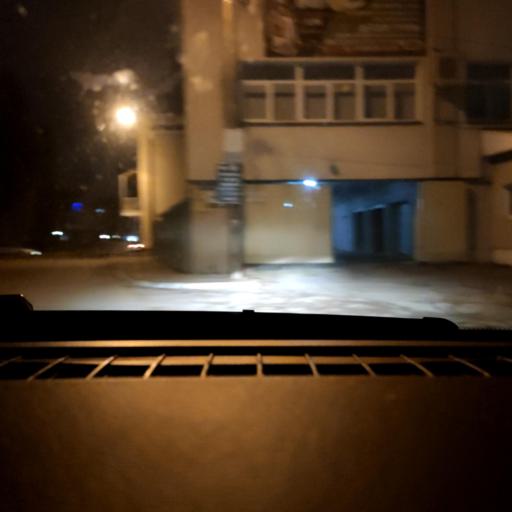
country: RU
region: Voronezj
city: Voronezh
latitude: 51.6670
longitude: 39.2448
